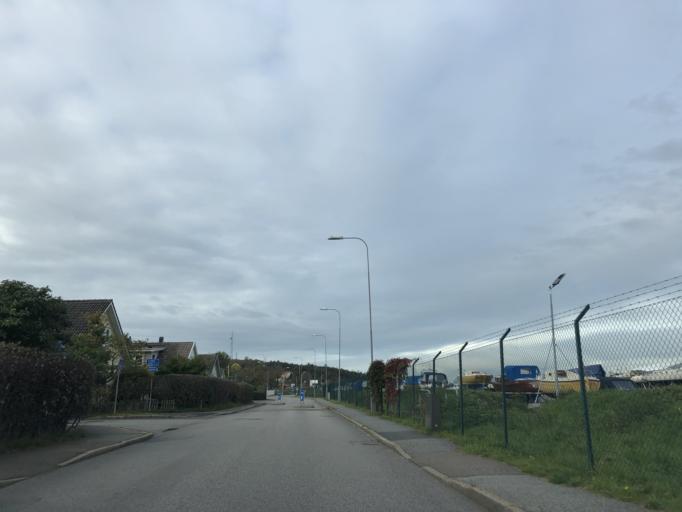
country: SE
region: Vaestra Goetaland
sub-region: Goteborg
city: Majorna
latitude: 57.6799
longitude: 11.8745
